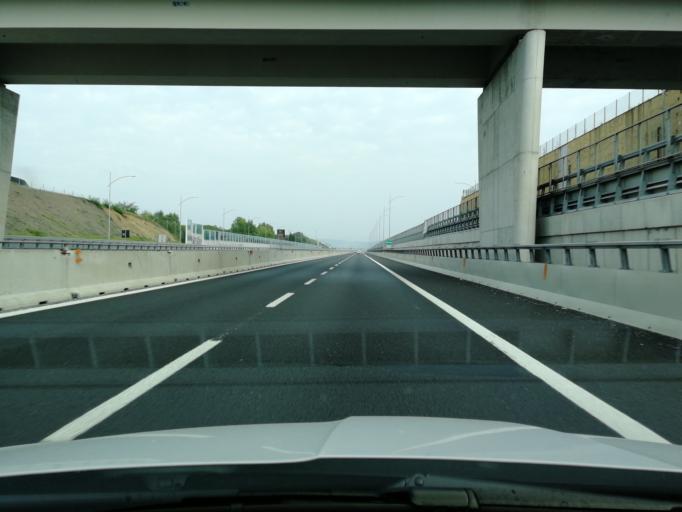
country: IT
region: Latium
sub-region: Citta metropolitana di Roma Capitale
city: Setteville
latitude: 41.9207
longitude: 12.6737
